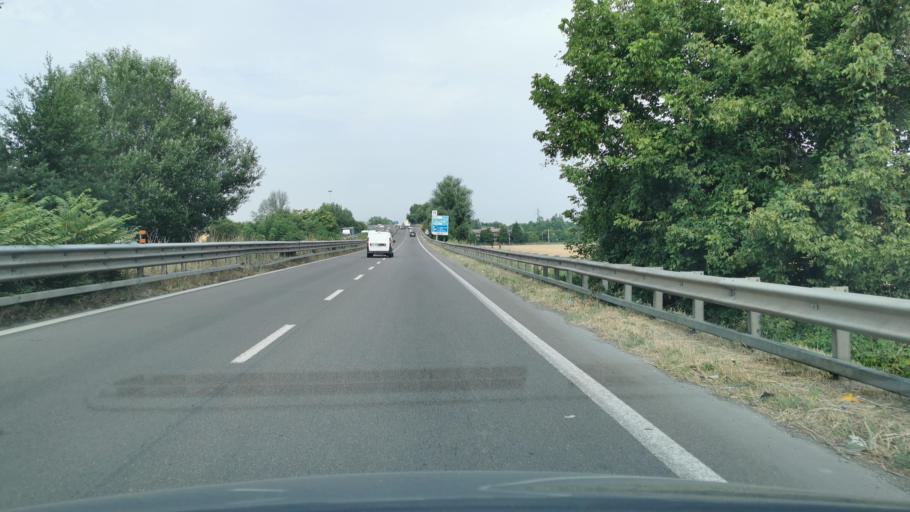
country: IT
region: Emilia-Romagna
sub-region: Provincia di Modena
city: Villanova
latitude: 44.6724
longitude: 10.9180
